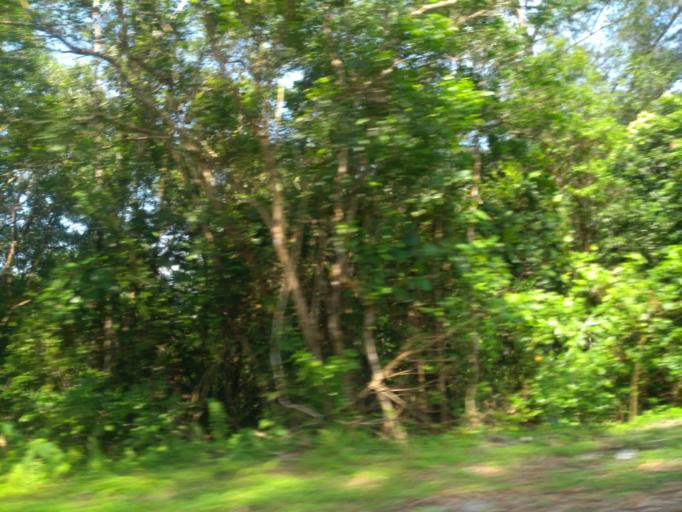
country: MY
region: Sarawak
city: Kuching
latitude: 1.7456
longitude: 110.3161
